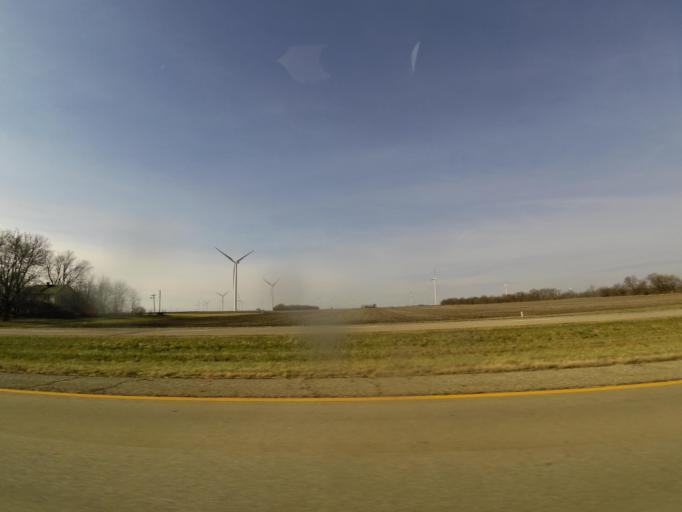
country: US
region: Illinois
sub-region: Macon County
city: Forsyth
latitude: 39.9842
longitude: -88.9560
